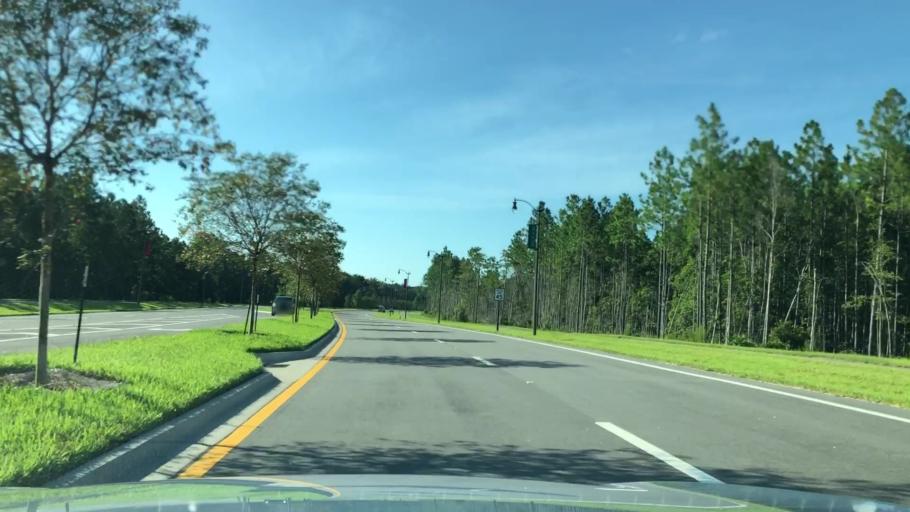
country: US
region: Florida
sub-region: Saint Johns County
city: Palm Valley
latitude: 30.0835
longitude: -81.4047
